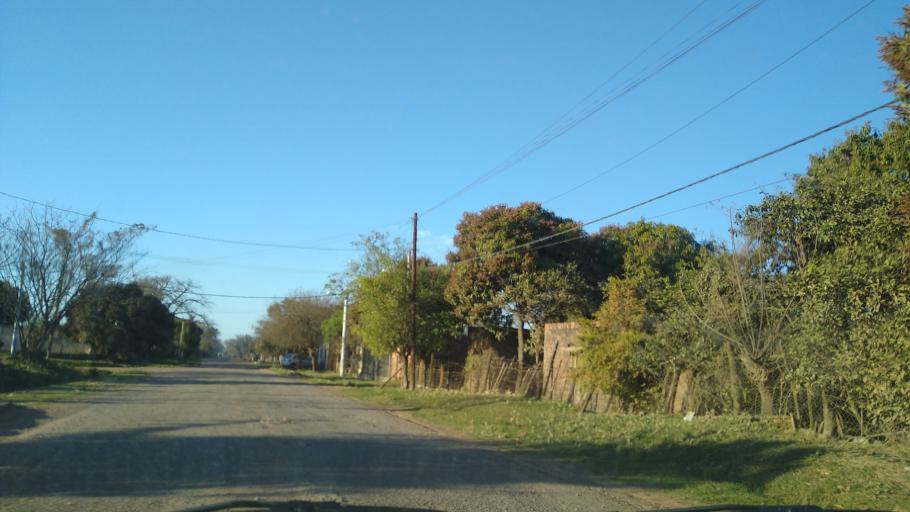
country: AR
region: Chaco
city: Barranqueras
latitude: -27.4682
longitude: -58.9494
